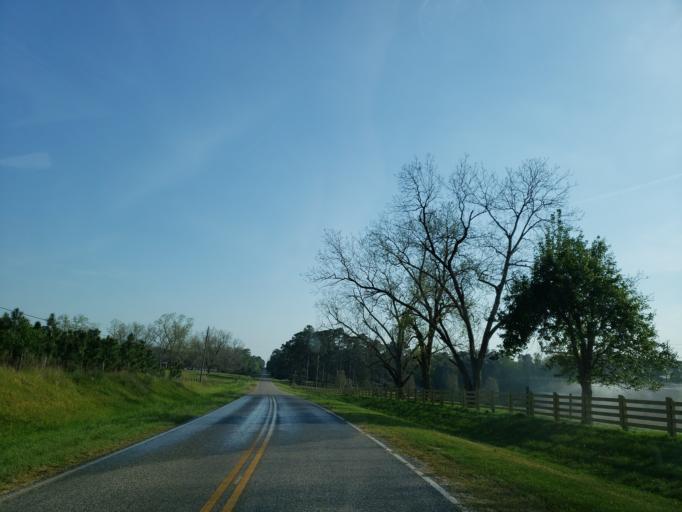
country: US
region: Georgia
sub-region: Tift County
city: Tifton
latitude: 31.5303
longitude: -83.5597
